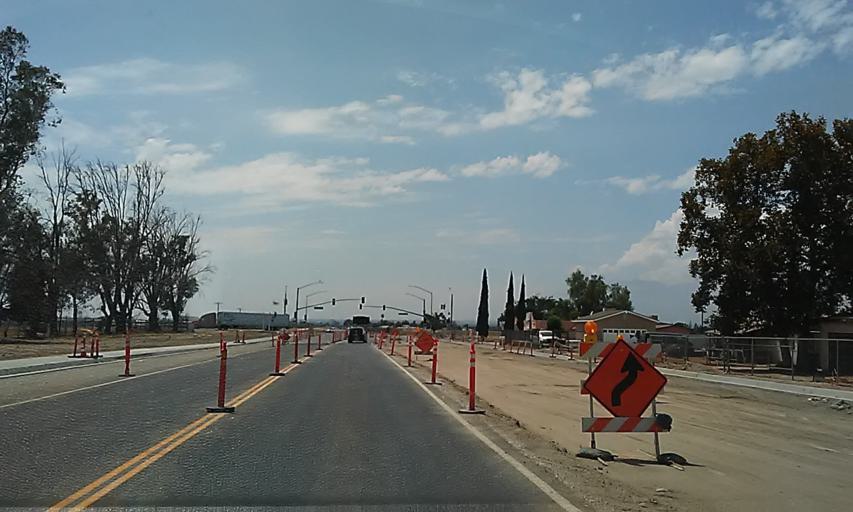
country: US
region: California
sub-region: San Bernardino County
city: Highland
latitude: 34.1067
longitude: -117.2243
